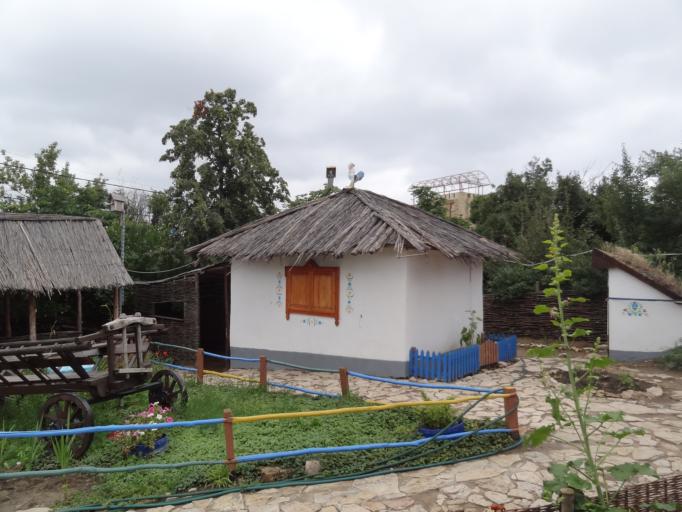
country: RU
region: Saratov
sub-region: Saratovskiy Rayon
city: Saratov
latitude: 51.5412
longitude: 46.0613
